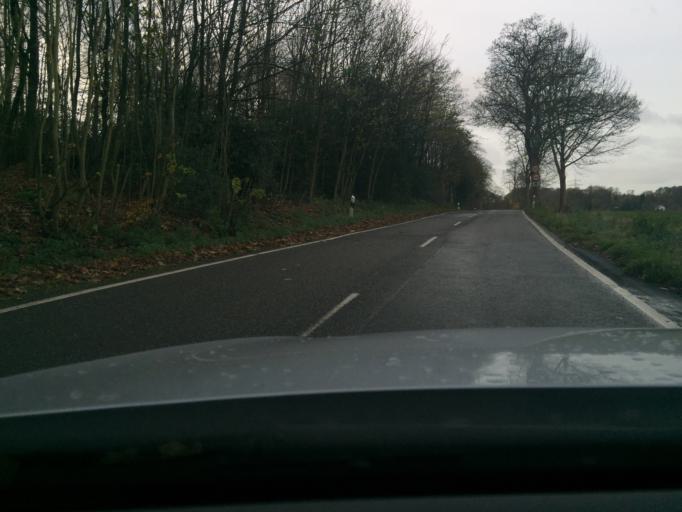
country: DE
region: North Rhine-Westphalia
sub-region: Regierungsbezirk Dusseldorf
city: Velbert
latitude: 51.3755
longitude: 7.0706
